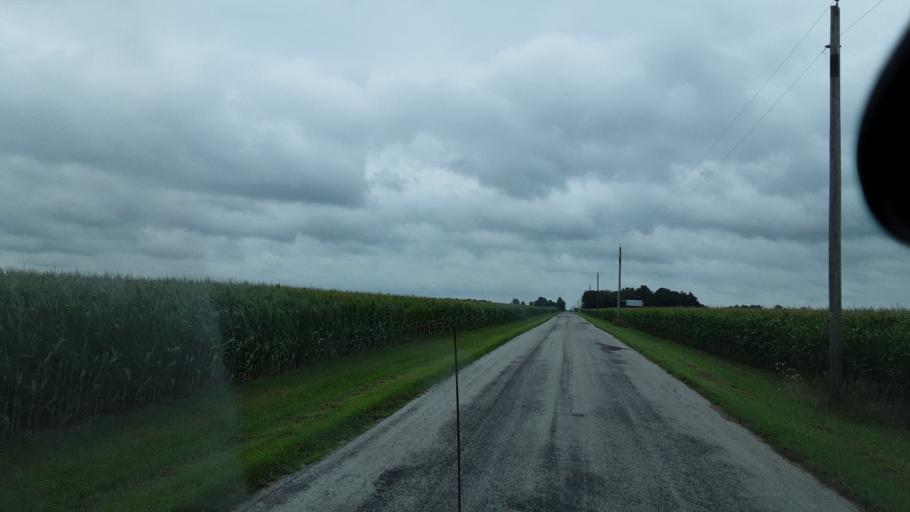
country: US
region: Indiana
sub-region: Wells County
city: Bluffton
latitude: 40.7999
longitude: -85.0715
